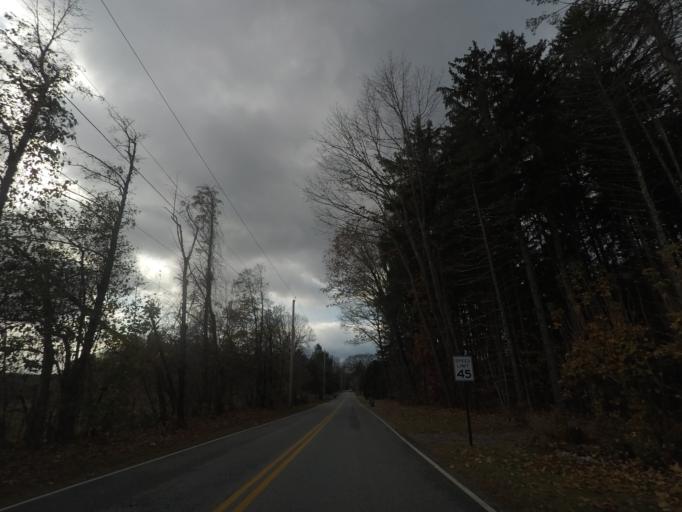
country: US
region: New York
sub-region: Saratoga County
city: Ballston Spa
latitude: 43.0119
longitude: -73.8055
